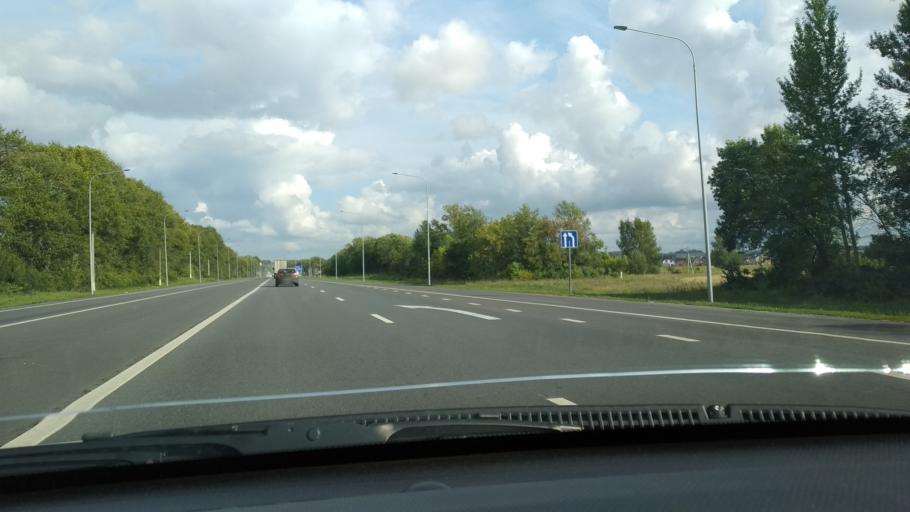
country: RU
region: Tatarstan
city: Stolbishchi
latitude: 55.6592
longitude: 49.3032
